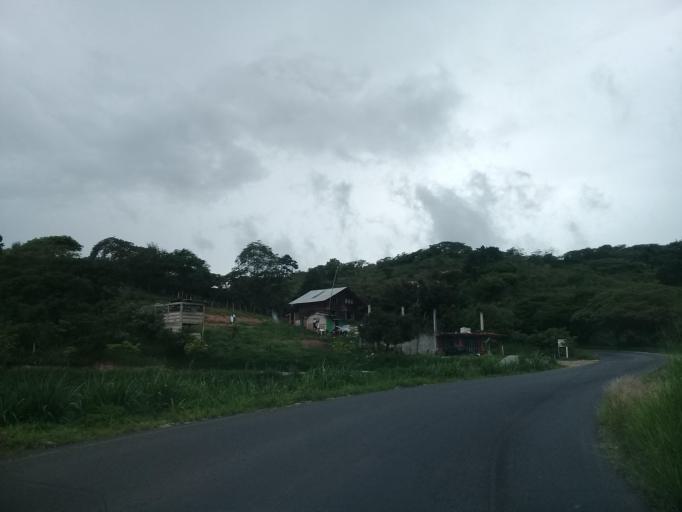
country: MX
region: Veracruz
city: El Castillo
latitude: 19.5604
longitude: -96.8513
